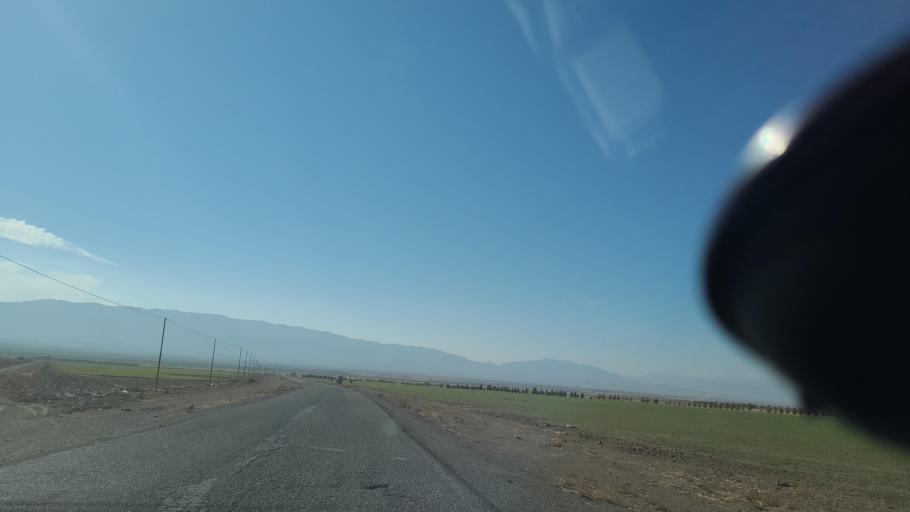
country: IR
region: Razavi Khorasan
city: Dowlatabad
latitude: 35.6098
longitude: 59.4683
